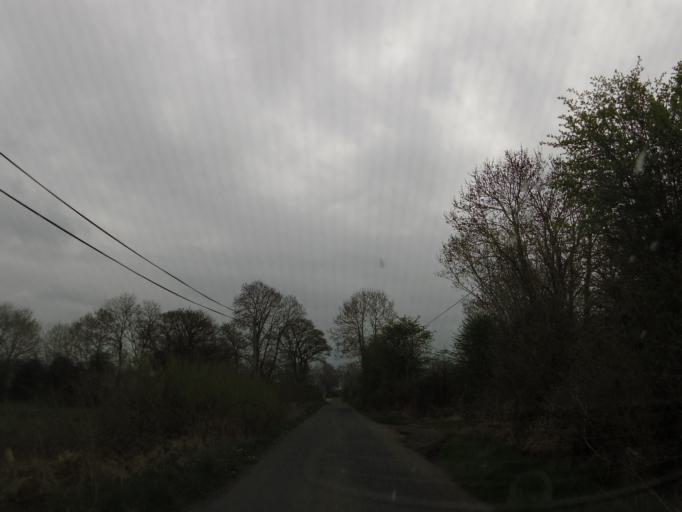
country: IE
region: Connaught
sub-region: Maigh Eo
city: Kiltamagh
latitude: 53.7981
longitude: -8.9680
